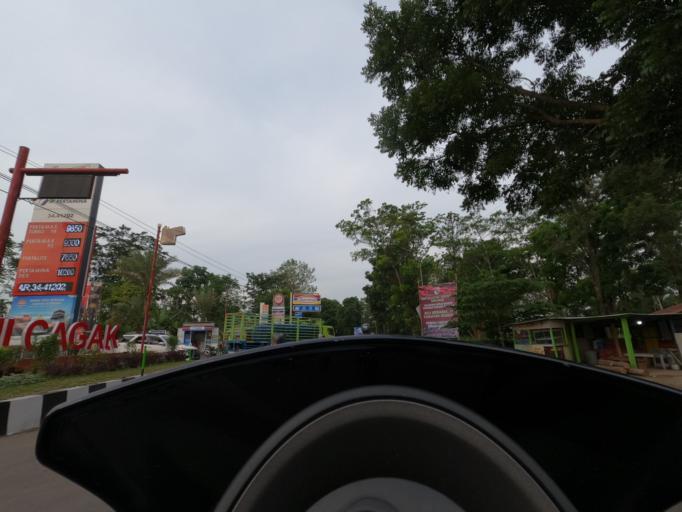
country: ID
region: West Java
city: Lembang
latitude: -6.6761
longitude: 107.6931
